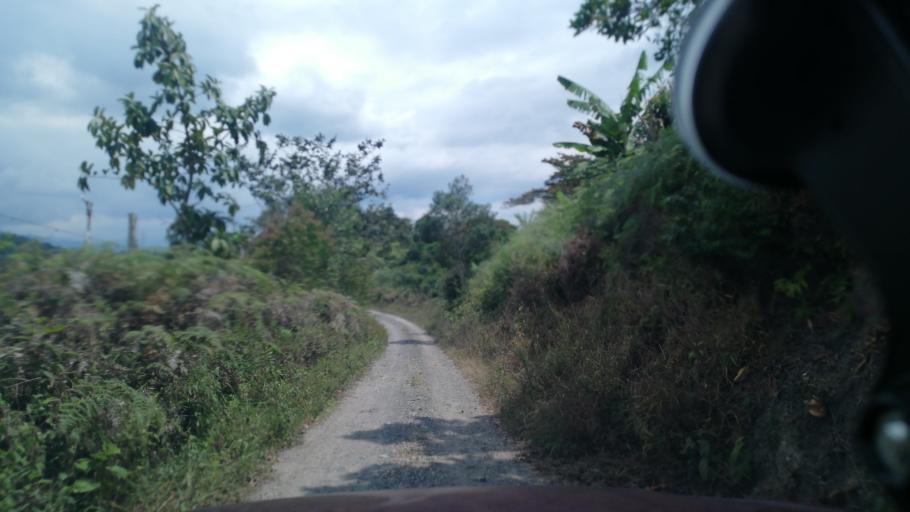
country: CO
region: Cundinamarca
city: Vergara
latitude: 5.1938
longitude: -74.2744
